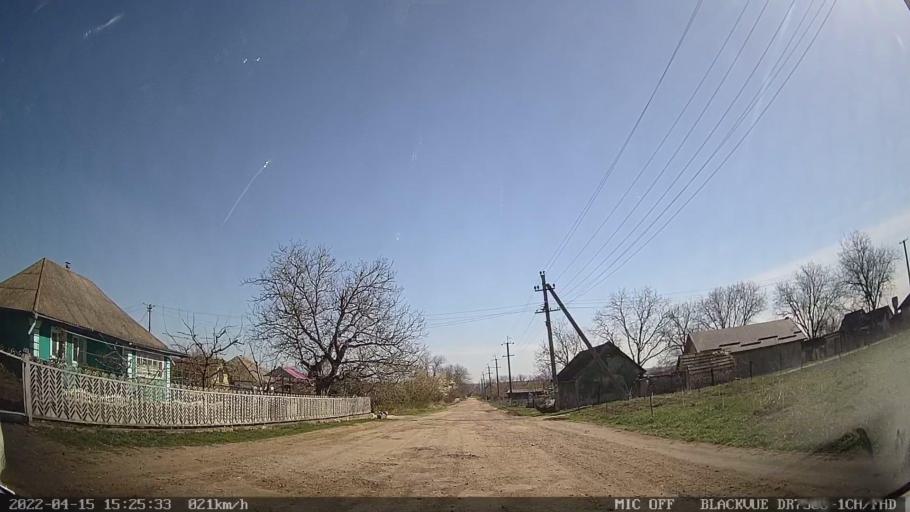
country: MD
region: Raionul Ocnita
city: Otaci
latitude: 48.3647
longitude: 27.9266
